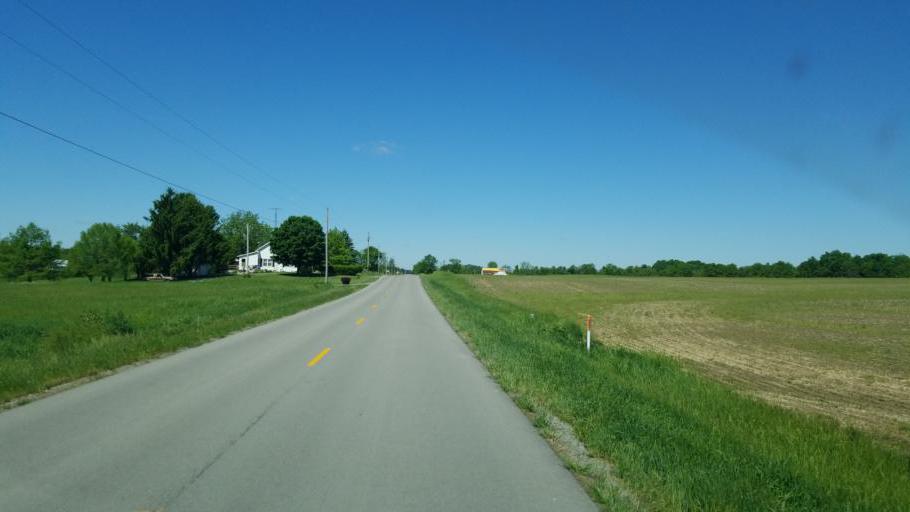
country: US
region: Ohio
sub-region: Logan County
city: Russells Point
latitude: 40.4249
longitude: -83.8656
